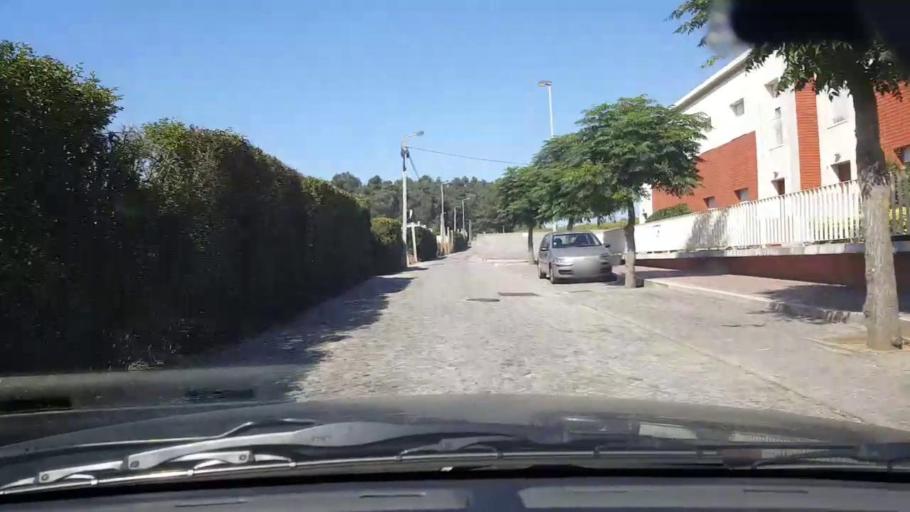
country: PT
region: Porto
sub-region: Matosinhos
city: Lavra
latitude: 41.2990
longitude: -8.7250
